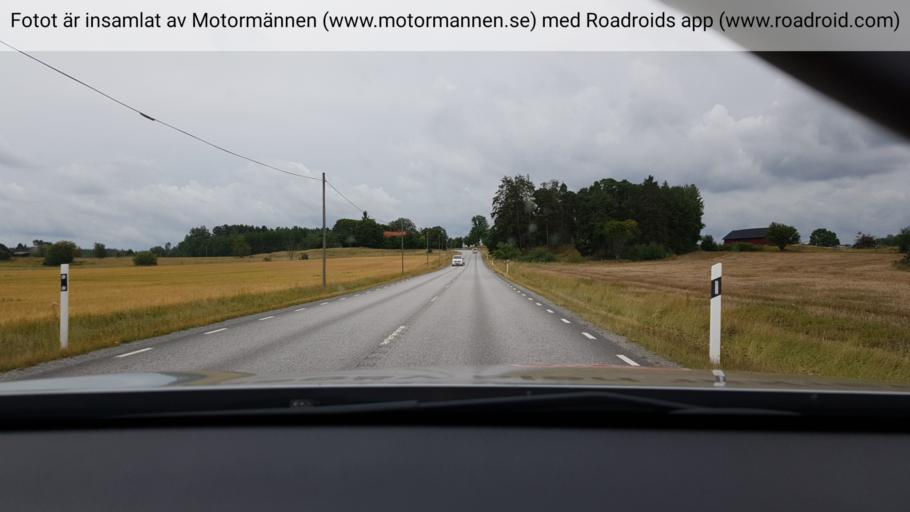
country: SE
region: Stockholm
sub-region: Vallentuna Kommun
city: Vallentuna
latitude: 59.6817
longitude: 18.0417
